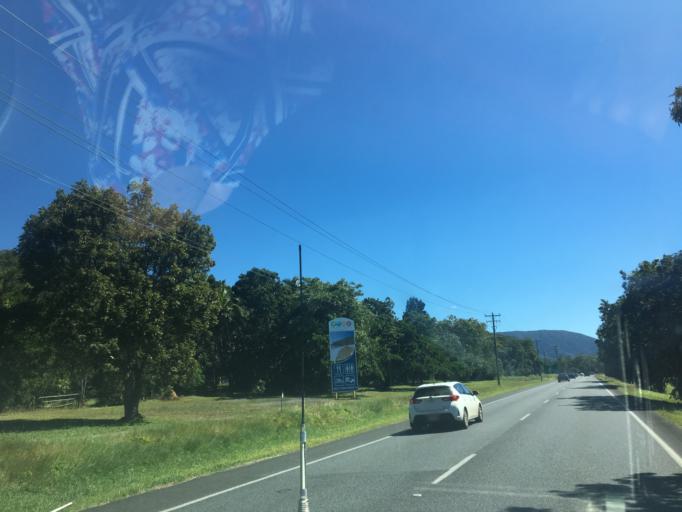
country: AU
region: Queensland
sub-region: Cairns
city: Trinity Beach
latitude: -16.8030
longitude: 145.6889
